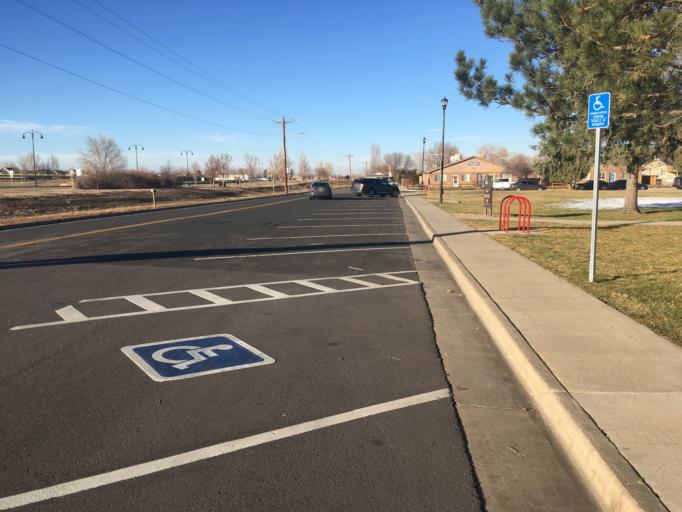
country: US
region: Colorado
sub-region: Weld County
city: Frederick
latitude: 40.0988
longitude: -104.9413
